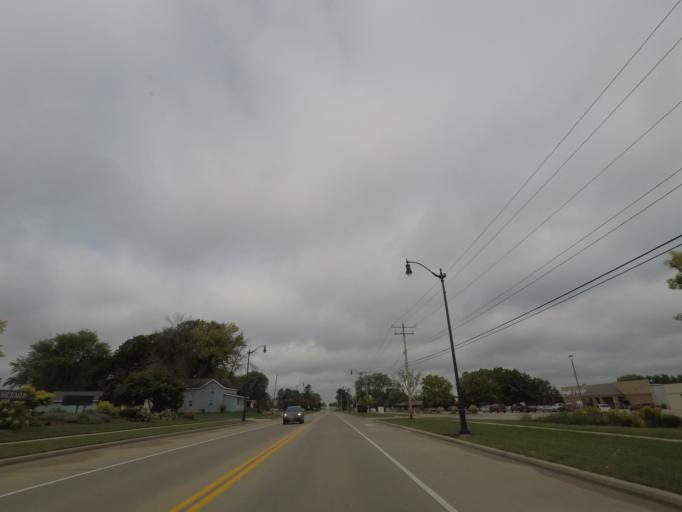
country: US
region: Wisconsin
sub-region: Jefferson County
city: Jefferson
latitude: 43.0060
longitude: -88.8244
